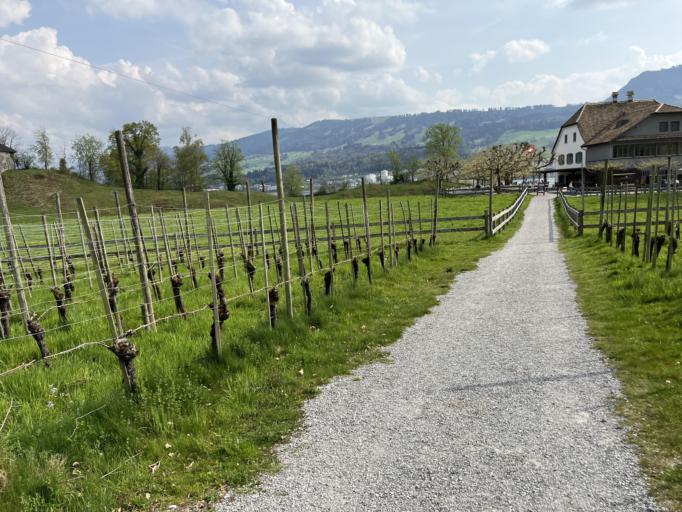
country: CH
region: Schwyz
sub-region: Bezirk Hoefe
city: Freienbach
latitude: 47.2177
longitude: 8.7786
